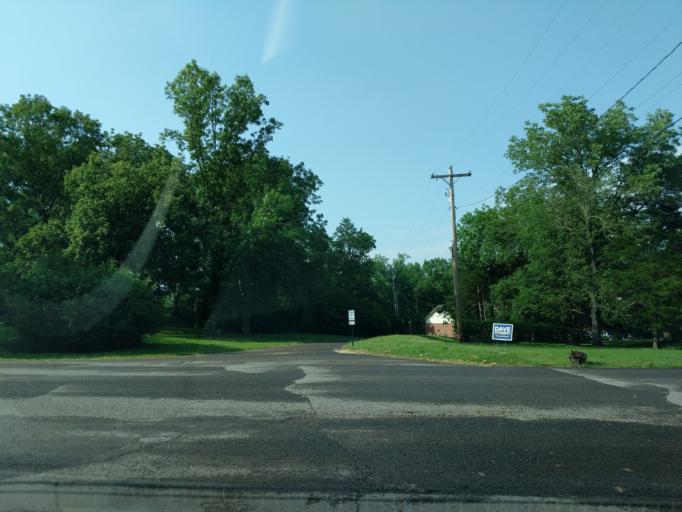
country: US
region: Tennessee
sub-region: Cheatham County
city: Pegram
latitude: 36.0410
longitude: -86.9573
